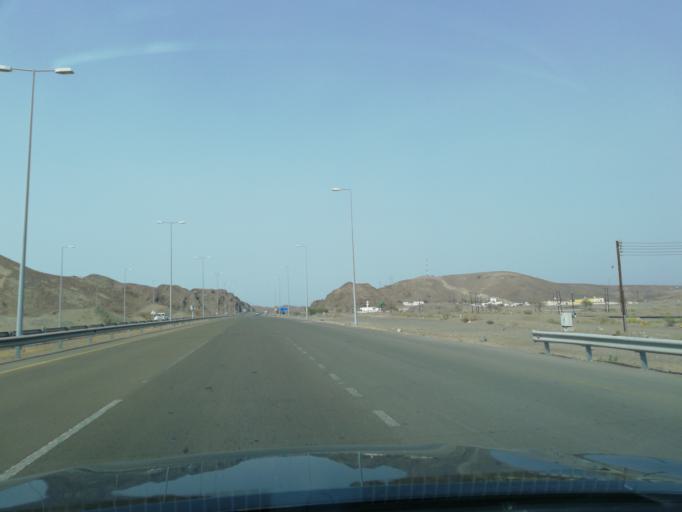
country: OM
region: Al Batinah
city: Al Liwa'
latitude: 24.3341
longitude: 56.4925
